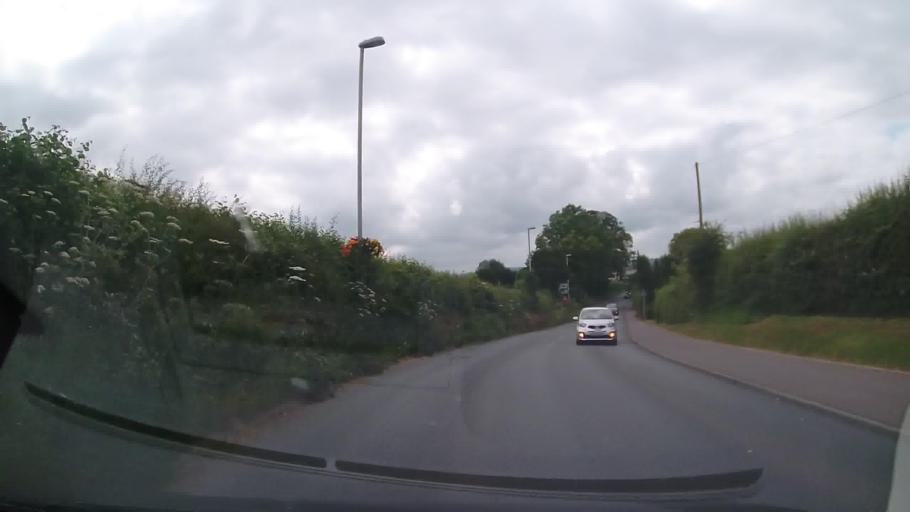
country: GB
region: England
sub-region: Shropshire
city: Gobowen
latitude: 52.9189
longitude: -3.0162
